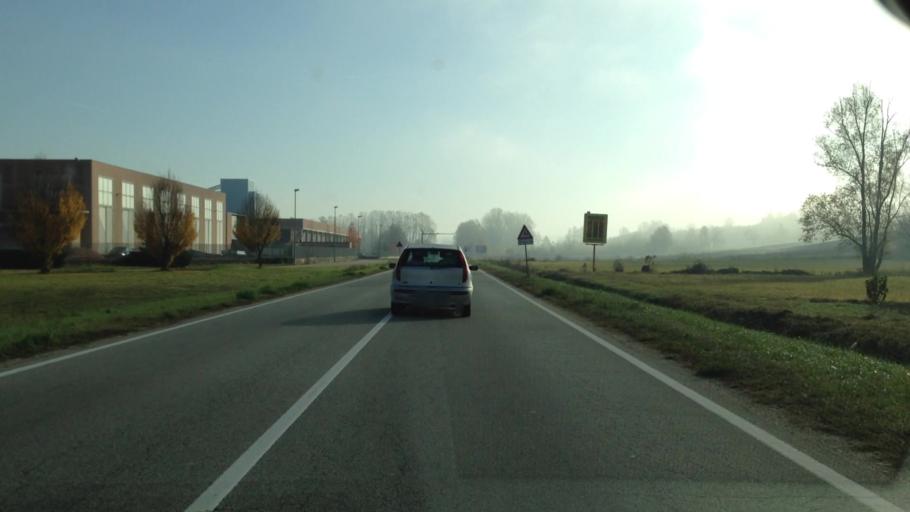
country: IT
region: Piedmont
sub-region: Provincia di Asti
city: Vigliano d'Asti
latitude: 44.8256
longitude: 8.2143
